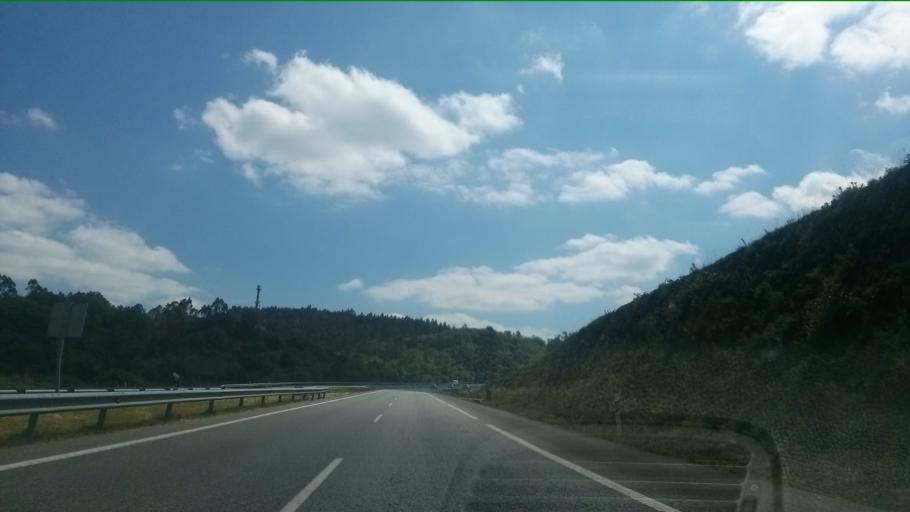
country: ES
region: Galicia
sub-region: Provincia da Coruna
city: Santiago de Compostela
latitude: 42.9018
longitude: -8.4673
